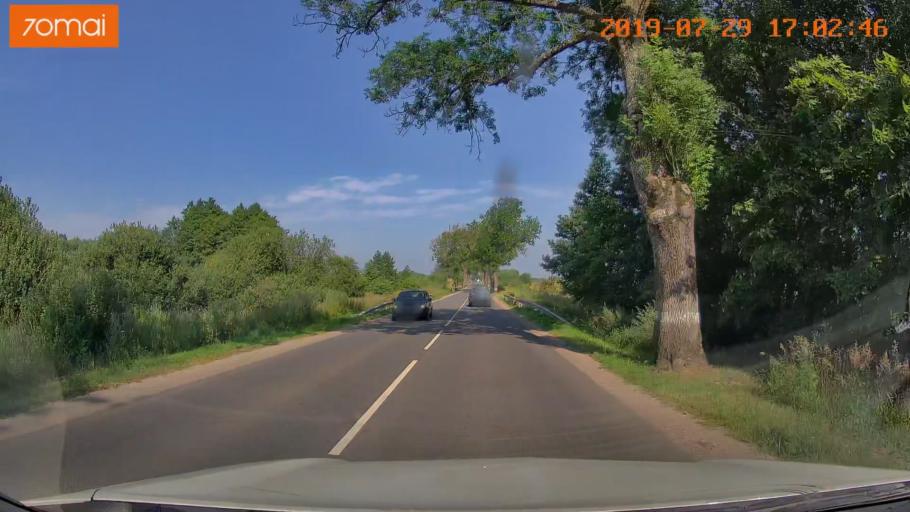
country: RU
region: Kaliningrad
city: Vzmorye
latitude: 54.8154
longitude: 20.2622
